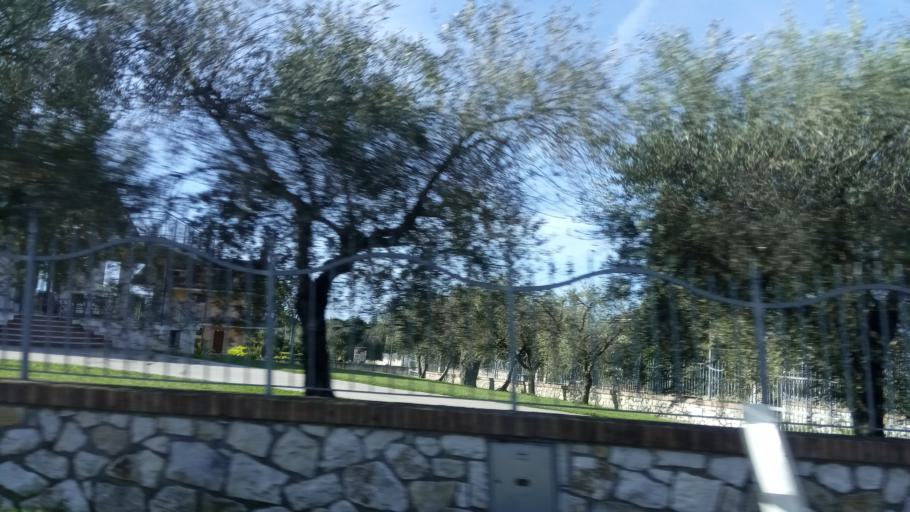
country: IT
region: Latium
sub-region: Provincia di Latina
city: Minturno
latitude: 41.2593
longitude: 13.7580
